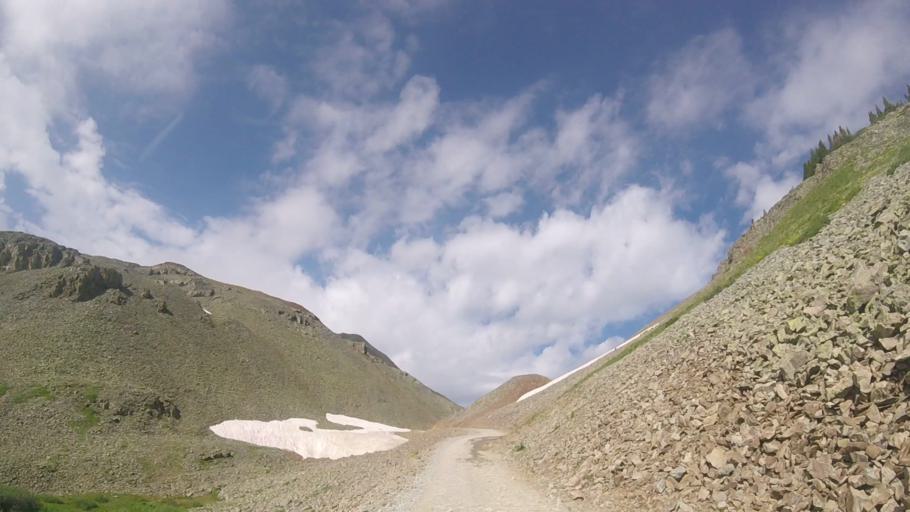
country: US
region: Colorado
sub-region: San Miguel County
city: Telluride
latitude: 37.8513
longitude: -107.7773
